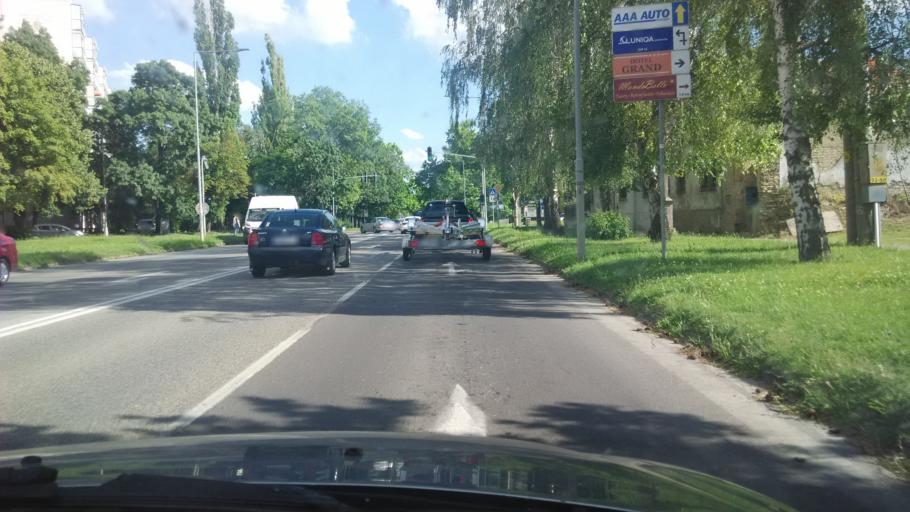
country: SK
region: Nitriansky
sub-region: Okres Nove Zamky
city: Nove Zamky
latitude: 47.9936
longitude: 18.1675
